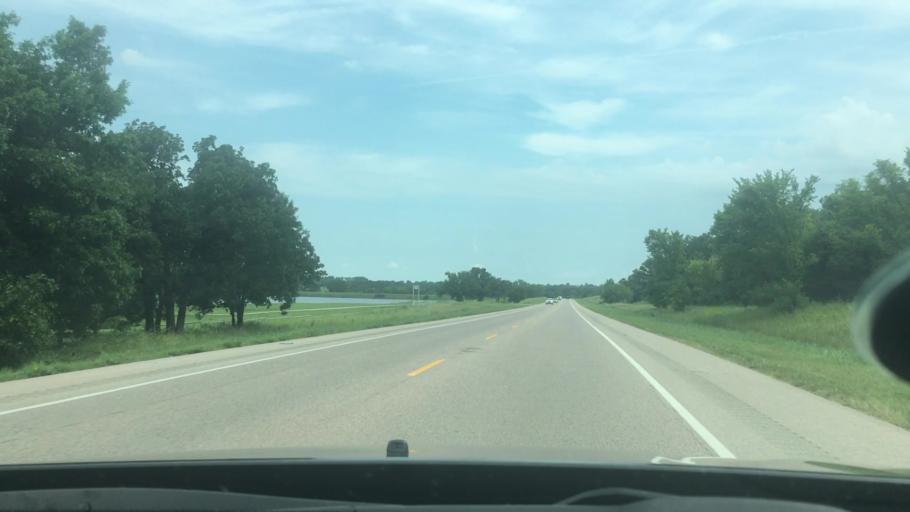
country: US
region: Oklahoma
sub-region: Seminole County
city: Seminole
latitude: 35.1648
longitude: -96.6743
